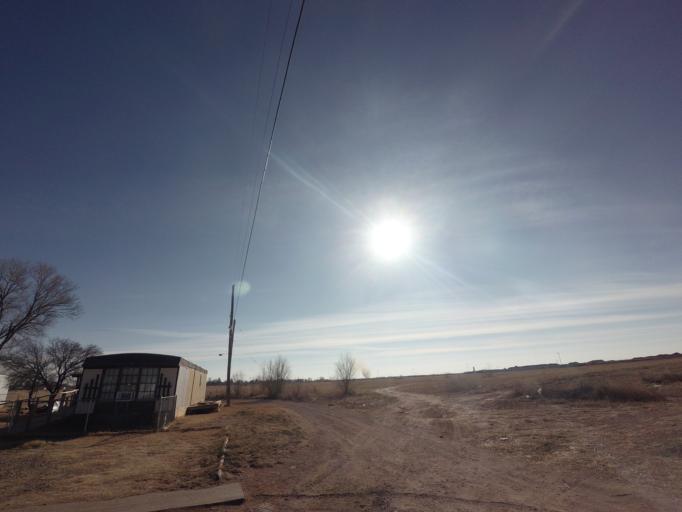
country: US
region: New Mexico
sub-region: Curry County
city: Clovis
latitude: 34.3871
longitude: -103.2031
